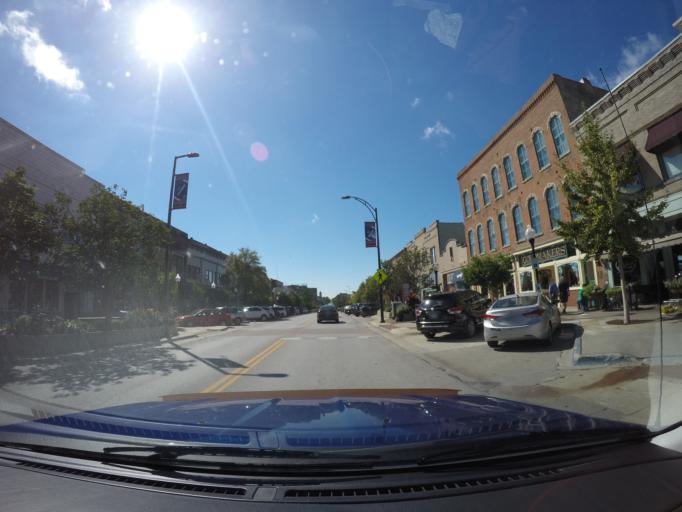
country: US
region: Kansas
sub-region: Douglas County
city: Lawrence
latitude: 38.9705
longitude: -95.2360
